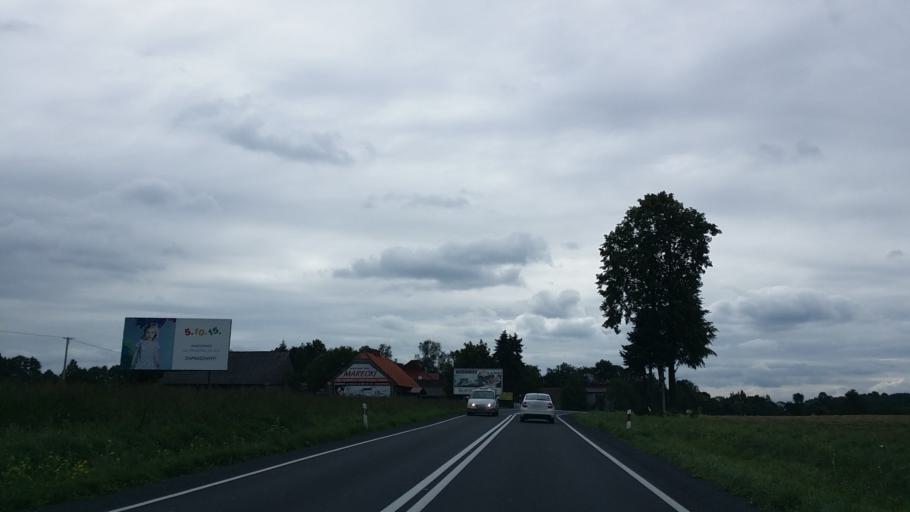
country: PL
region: Lesser Poland Voivodeship
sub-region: Powiat wadowicki
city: Radocza
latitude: 49.9436
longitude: 19.4514
